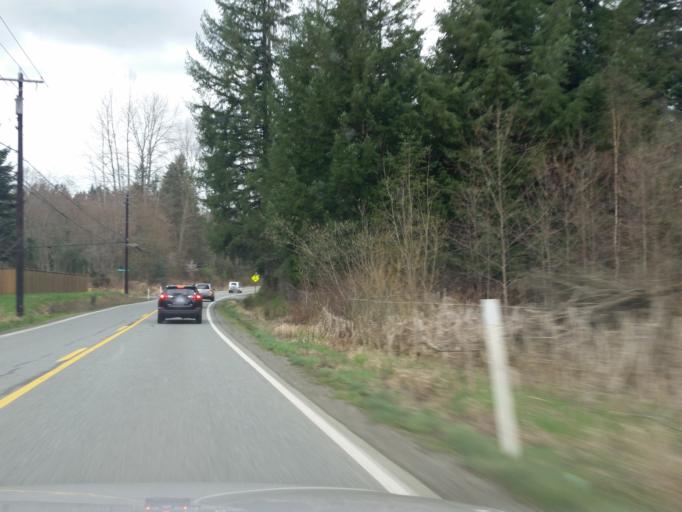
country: US
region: Washington
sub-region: Snohomish County
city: North Creek
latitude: 47.8051
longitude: -122.1581
